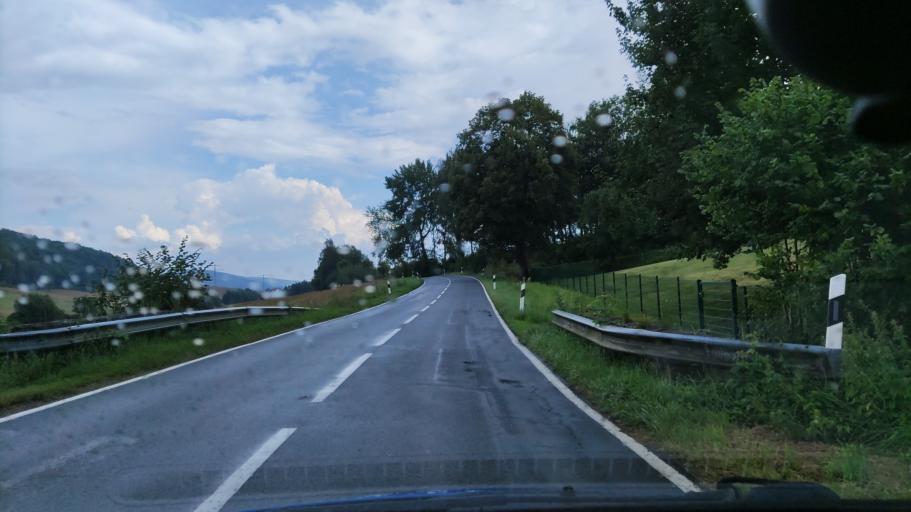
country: DE
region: Lower Saxony
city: Delligsen
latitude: 51.9571
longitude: 9.7858
